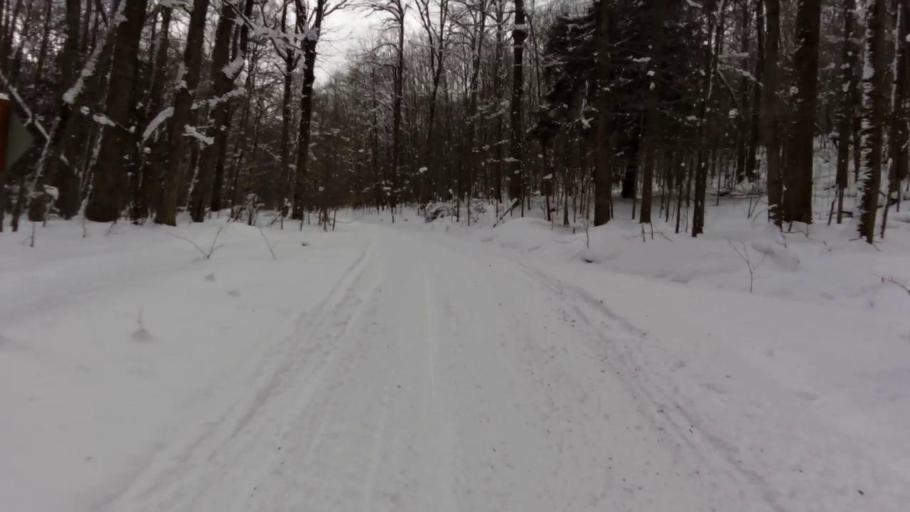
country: US
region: New York
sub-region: Cattaraugus County
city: Salamanca
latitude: 42.0613
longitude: -78.7793
